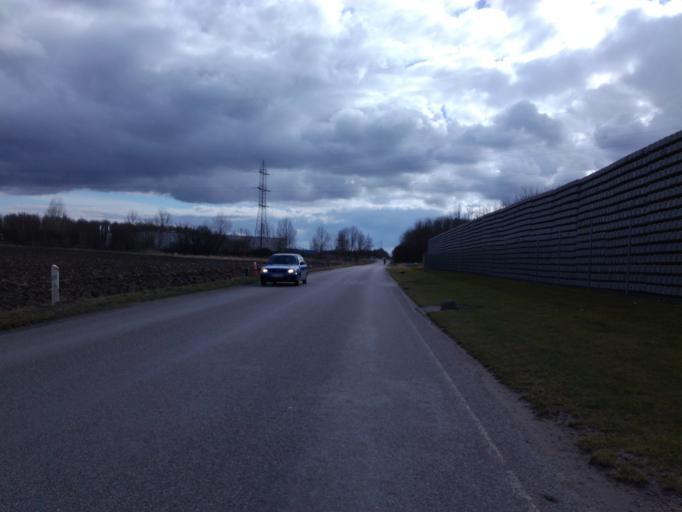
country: DK
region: South Denmark
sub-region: Fredericia Kommune
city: Fredericia
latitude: 55.5885
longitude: 9.7350
